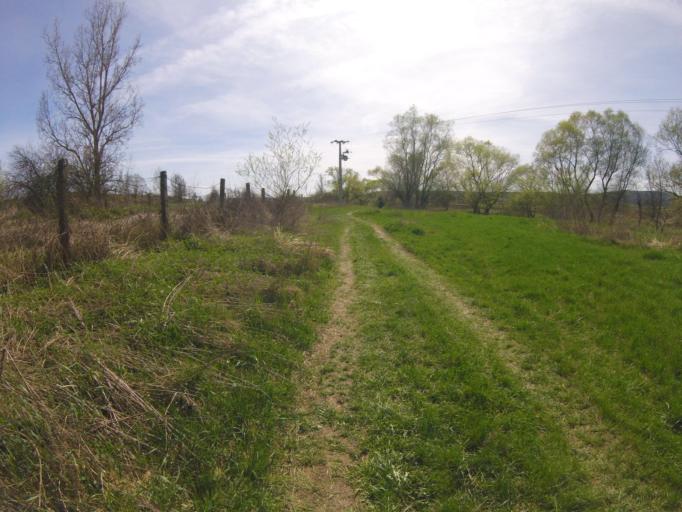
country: HU
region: Borsod-Abauj-Zemplen
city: Szendro
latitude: 48.4185
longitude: 20.7282
